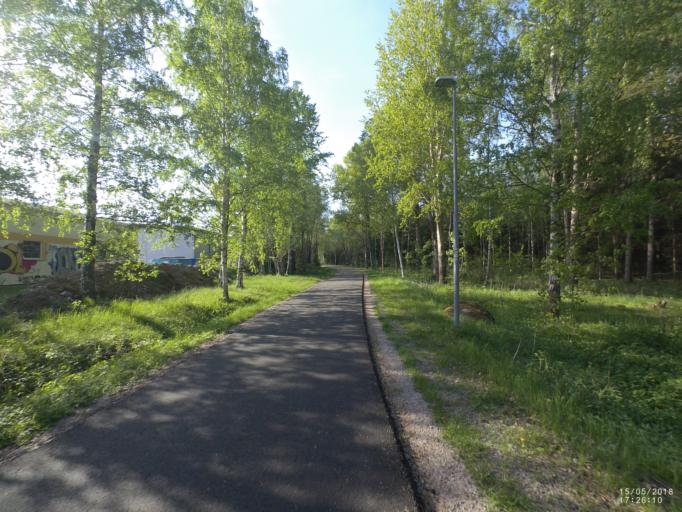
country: SE
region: Soedermanland
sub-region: Nykopings Kommun
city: Nykoping
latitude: 58.7208
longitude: 17.0271
